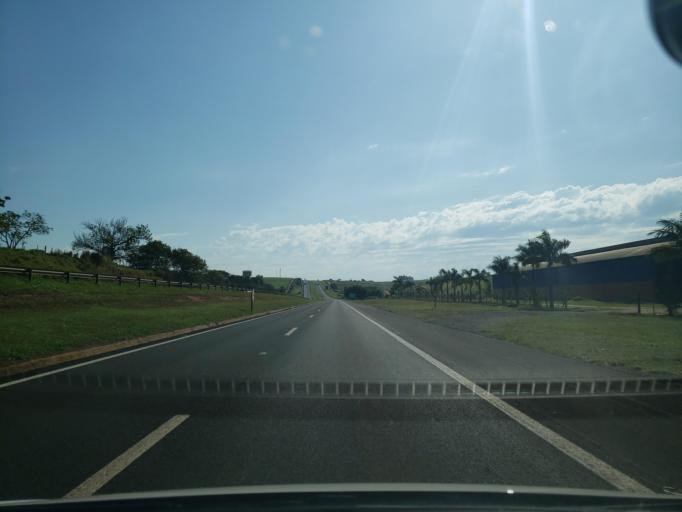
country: BR
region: Sao Paulo
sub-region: Penapolis
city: Penapolis
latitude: -21.5199
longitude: -50.0012
